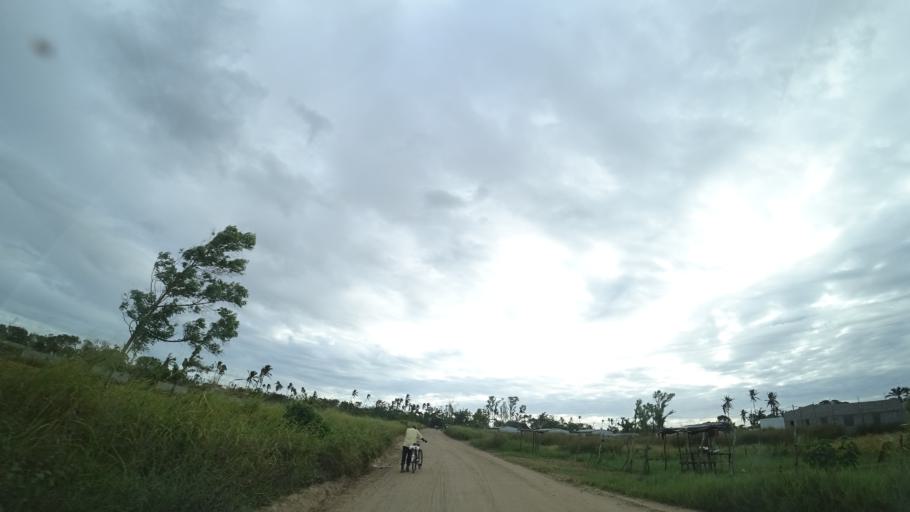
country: MZ
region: Sofala
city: Beira
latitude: -19.7640
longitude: 34.9000
